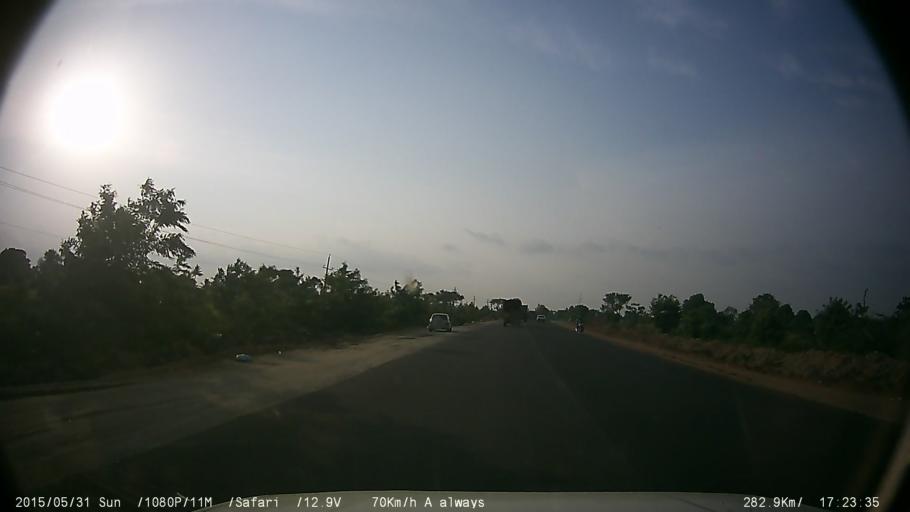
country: IN
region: Karnataka
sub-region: Chamrajnagar
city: Gundlupet
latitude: 11.8413
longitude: 76.6737
